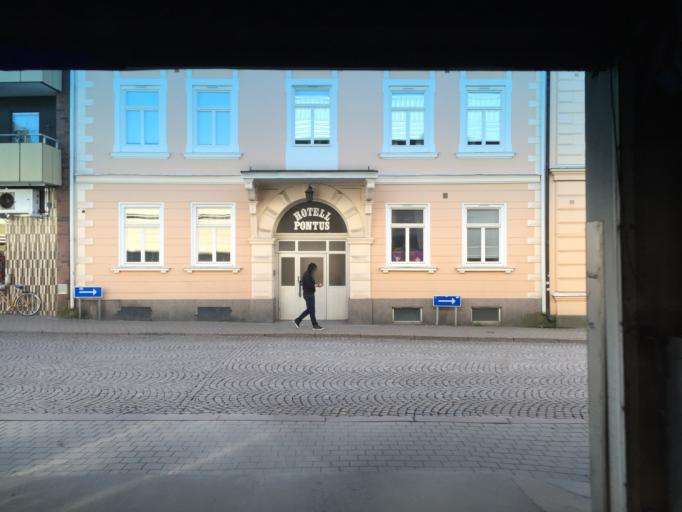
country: SE
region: Kalmar
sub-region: Oskarshamns Kommun
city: Oskarshamn
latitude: 57.2643
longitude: 16.4472
